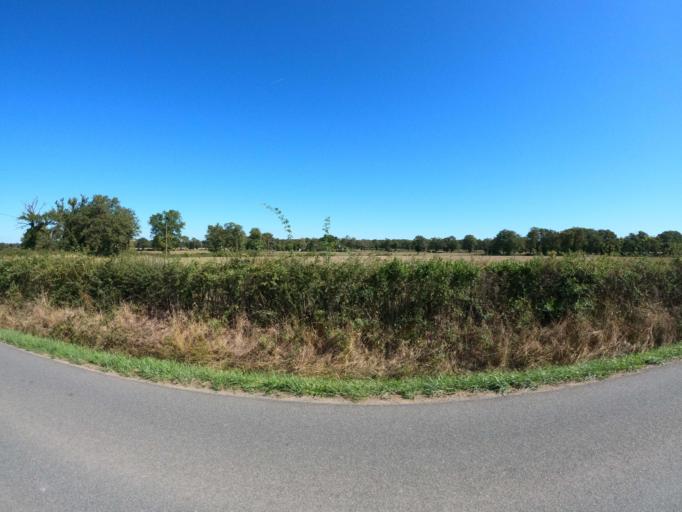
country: FR
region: Poitou-Charentes
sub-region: Departement de la Vienne
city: Lathus-Saint-Remy
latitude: 46.2862
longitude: 1.0074
